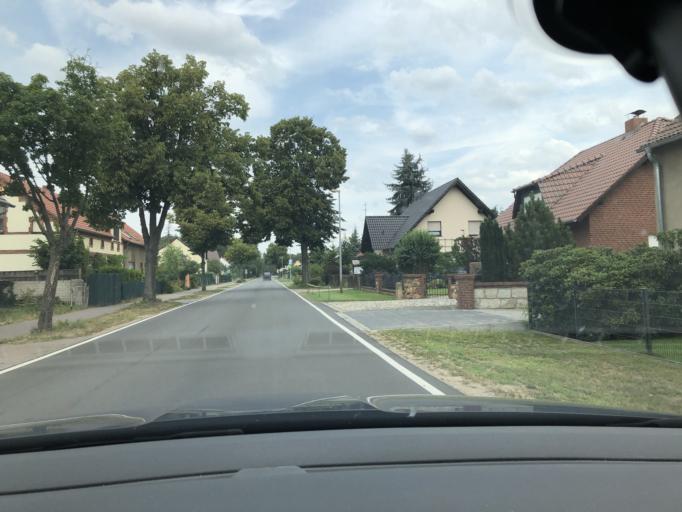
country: DE
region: Brandenburg
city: Kasel-Golzig
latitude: 51.9816
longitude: 13.7680
